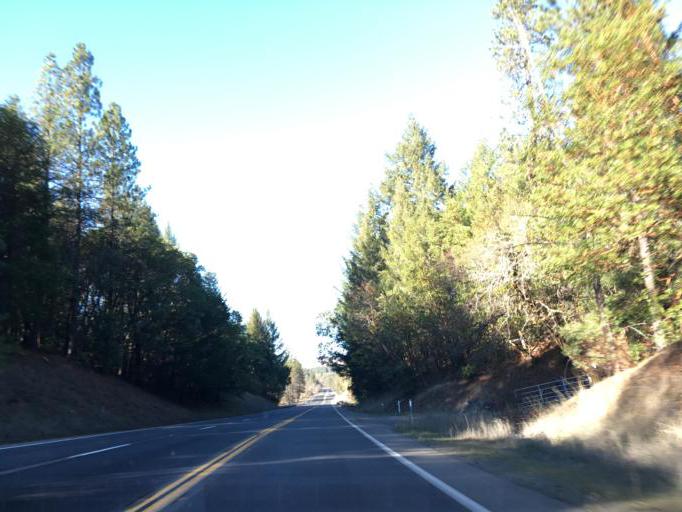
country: US
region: California
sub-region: Mendocino County
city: Laytonville
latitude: 39.7168
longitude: -123.4996
